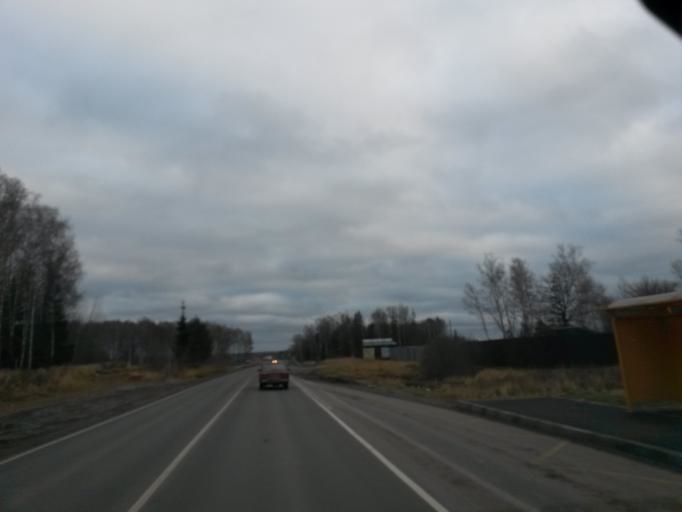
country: RU
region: Moskovskaya
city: Lyubuchany
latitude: 55.2447
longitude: 37.5248
